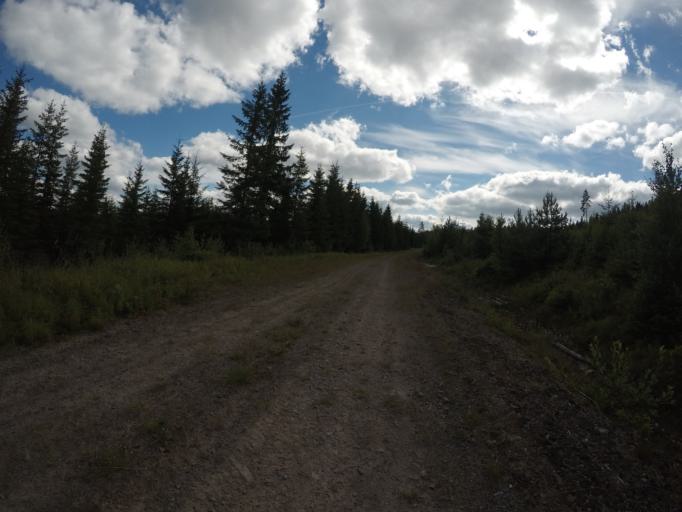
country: SE
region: Vaermland
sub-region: Filipstads Kommun
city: Lesjofors
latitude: 60.0803
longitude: 14.4600
